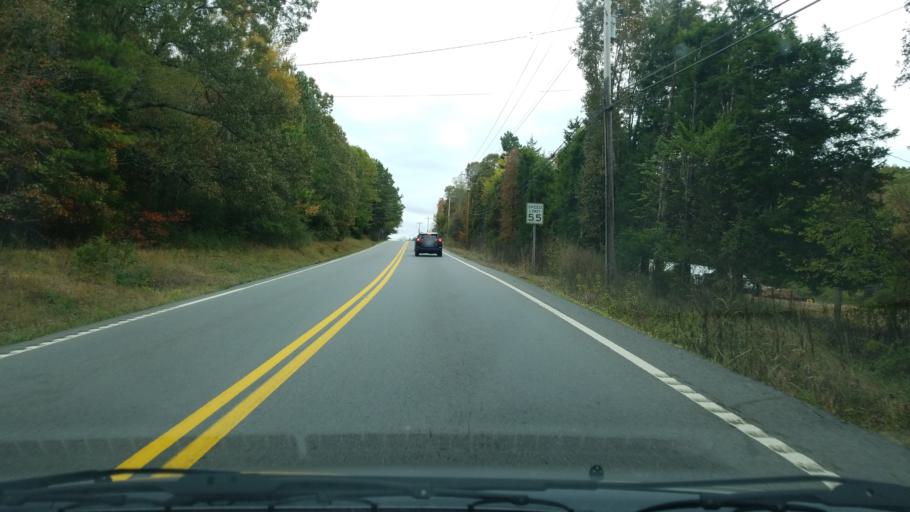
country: US
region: Tennessee
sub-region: Hamilton County
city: Sale Creek
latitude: 35.3520
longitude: -84.9904
